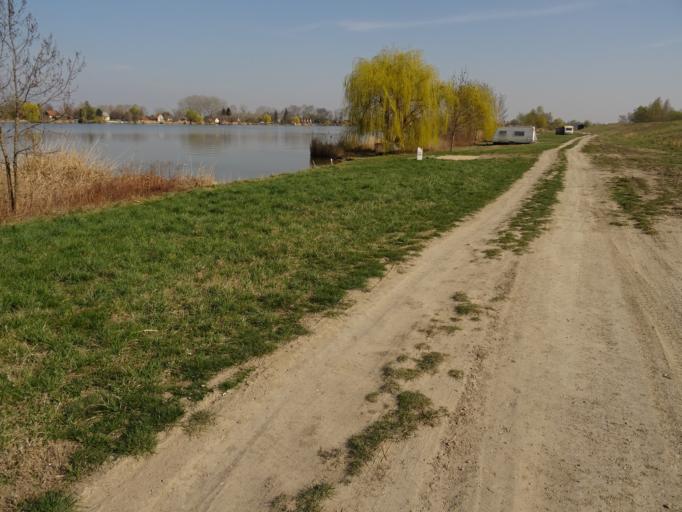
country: HU
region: Fejer
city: Racalmas
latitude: 47.0467
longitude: 18.9683
